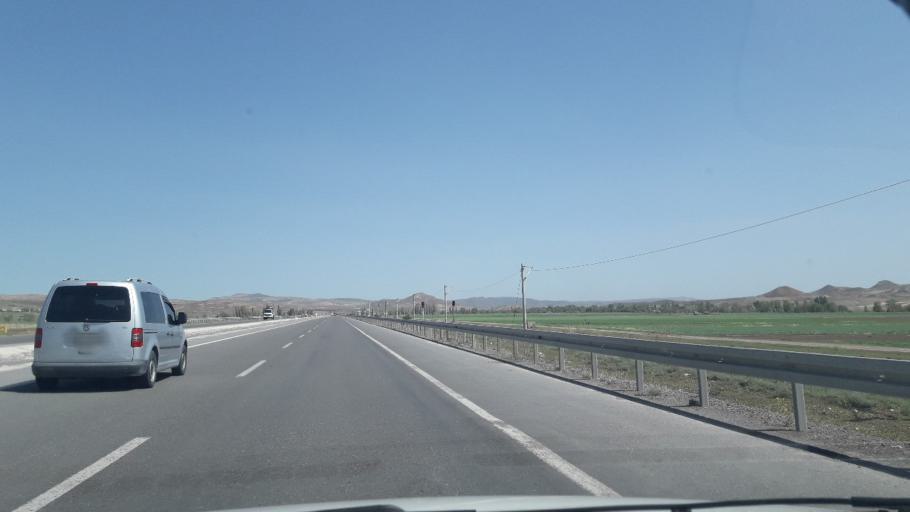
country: TR
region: Sivas
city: Ulas
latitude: 39.4942
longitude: 37.0092
